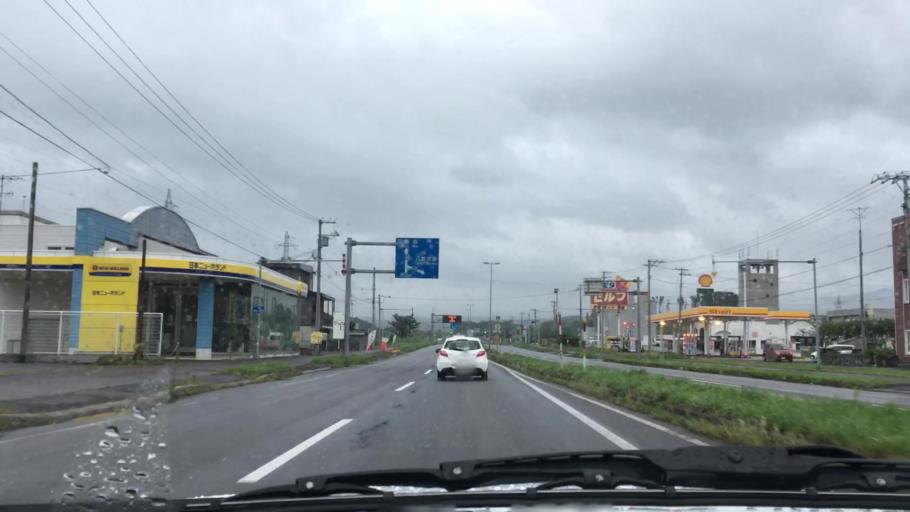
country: JP
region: Hokkaido
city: Nanae
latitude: 42.2486
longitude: 140.2873
